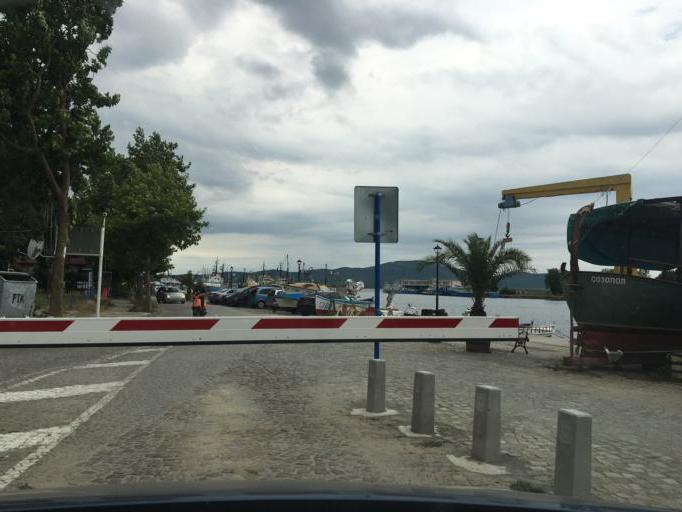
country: BG
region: Burgas
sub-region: Obshtina Sozopol
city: Sozopol
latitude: 42.4242
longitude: 27.6936
